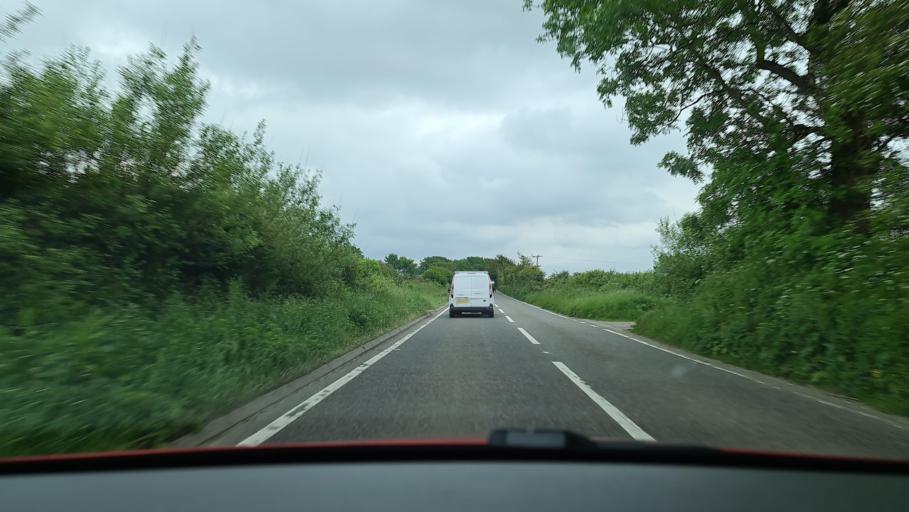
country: GB
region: England
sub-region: Cornwall
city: Camelford
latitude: 50.6307
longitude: -4.6655
